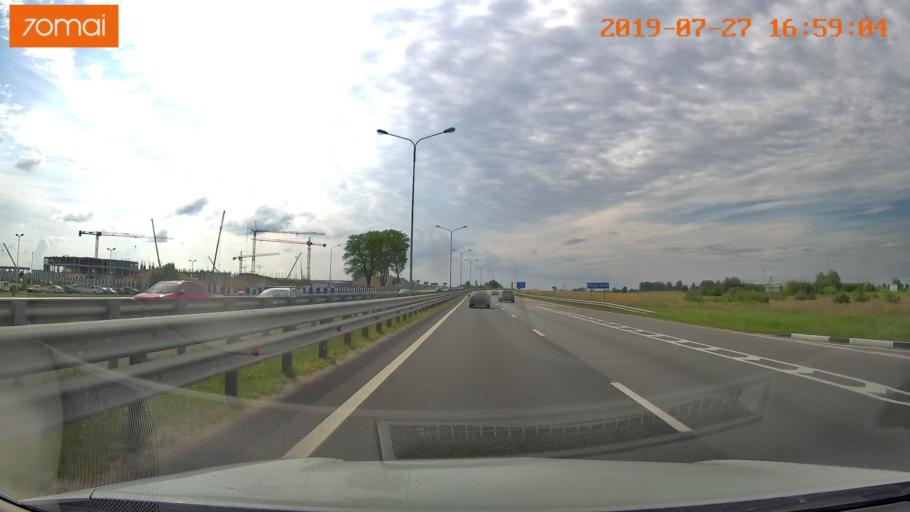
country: RU
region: Kaliningrad
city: Bol'shoe Isakovo
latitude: 54.7022
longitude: 20.6610
